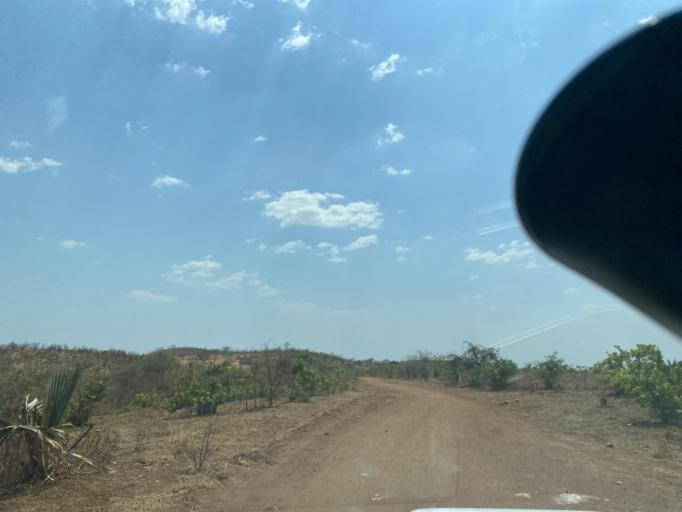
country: ZM
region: Lusaka
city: Lusaka
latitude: -15.4990
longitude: 27.9479
